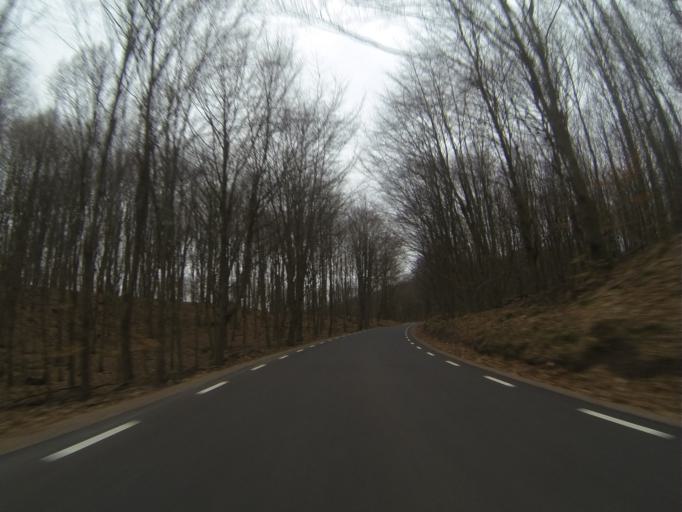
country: SE
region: Skane
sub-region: Lunds Kommun
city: Genarp
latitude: 55.5712
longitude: 13.4329
